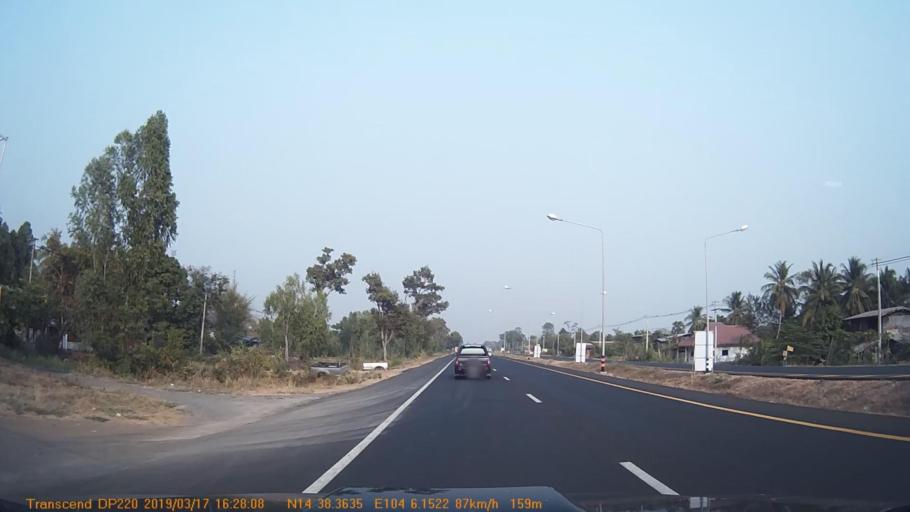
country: TH
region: Sisaket
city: Phu Sing
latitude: 14.6394
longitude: 104.1029
